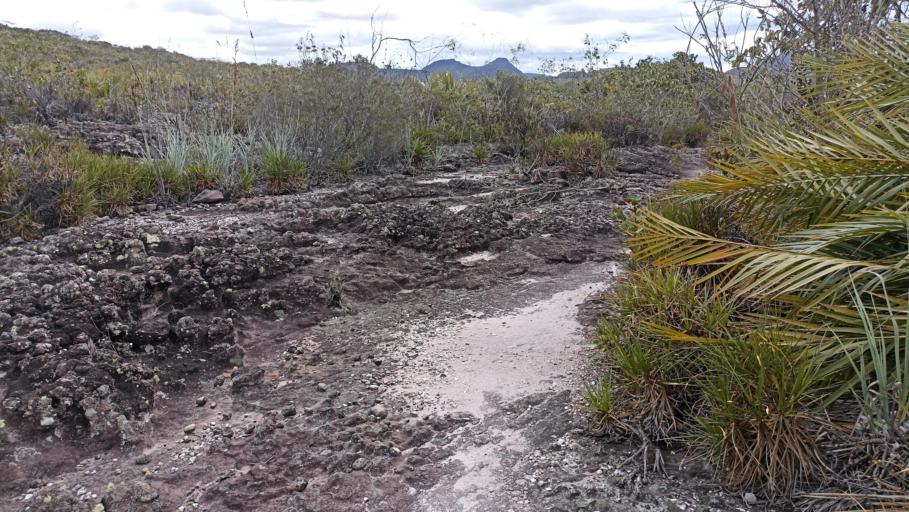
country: BR
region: Bahia
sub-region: Andarai
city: Vera Cruz
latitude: -12.9933
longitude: -41.3700
